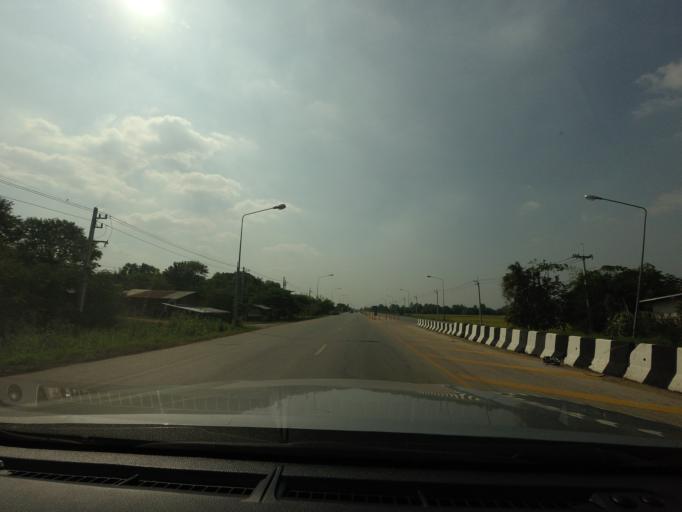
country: TH
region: Phitsanulok
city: Bang Rakam
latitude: 16.7680
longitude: 100.1466
